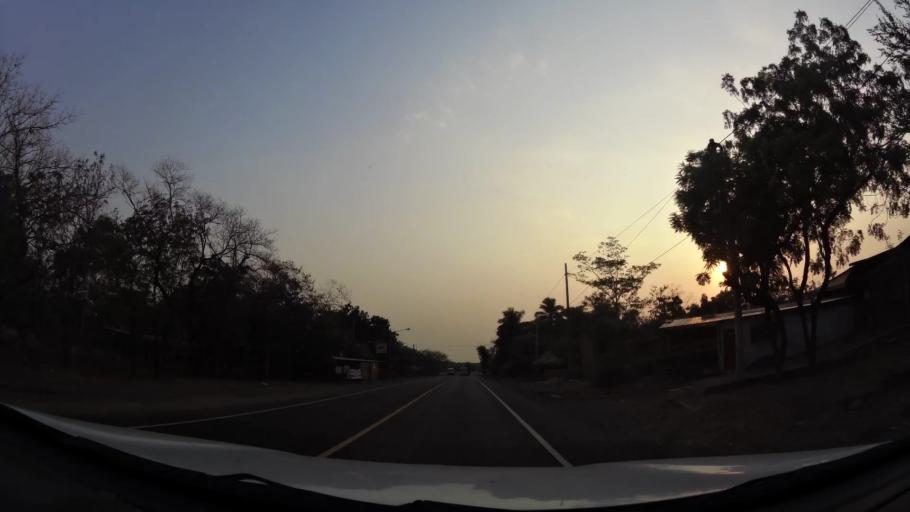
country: NI
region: Leon
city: La Paz Centro
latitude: 12.3361
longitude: -86.6657
